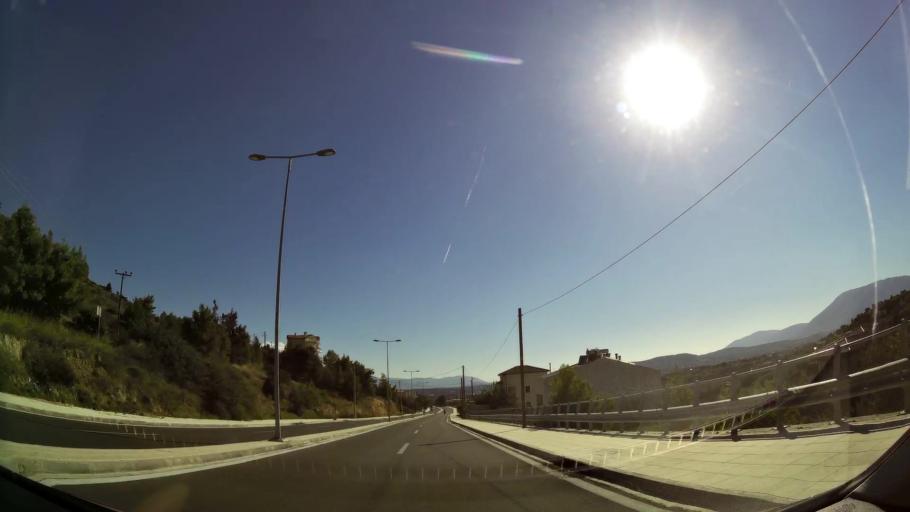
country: GR
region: Attica
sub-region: Nomarchia Anatolikis Attikis
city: Dhrafi
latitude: 38.0141
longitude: 23.9108
